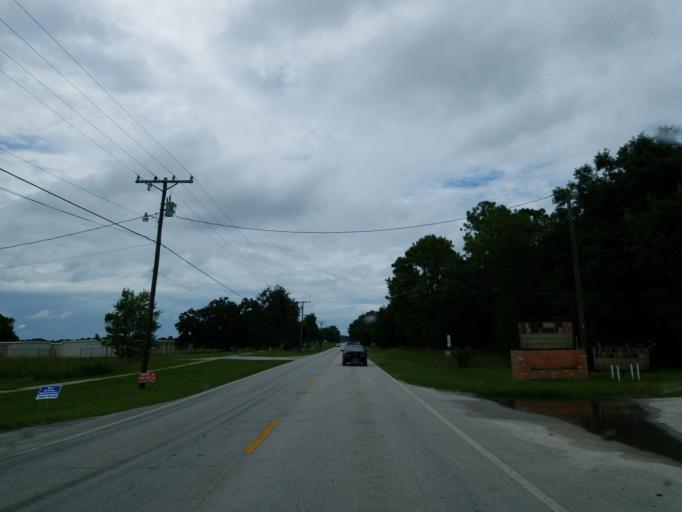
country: US
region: Florida
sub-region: Sumter County
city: Lake Panasoffkee
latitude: 28.7754
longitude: -82.1235
